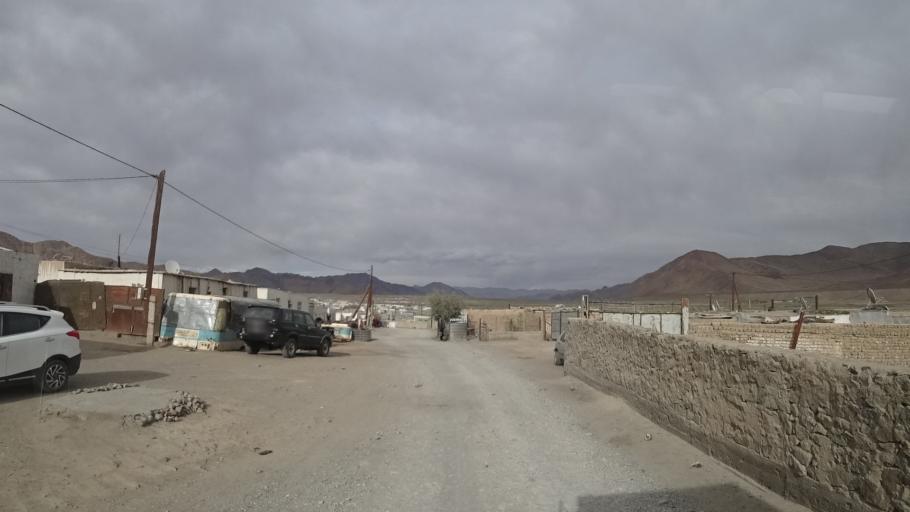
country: TJ
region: Gorno-Badakhshan
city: Murghob
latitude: 38.1742
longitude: 73.9703
